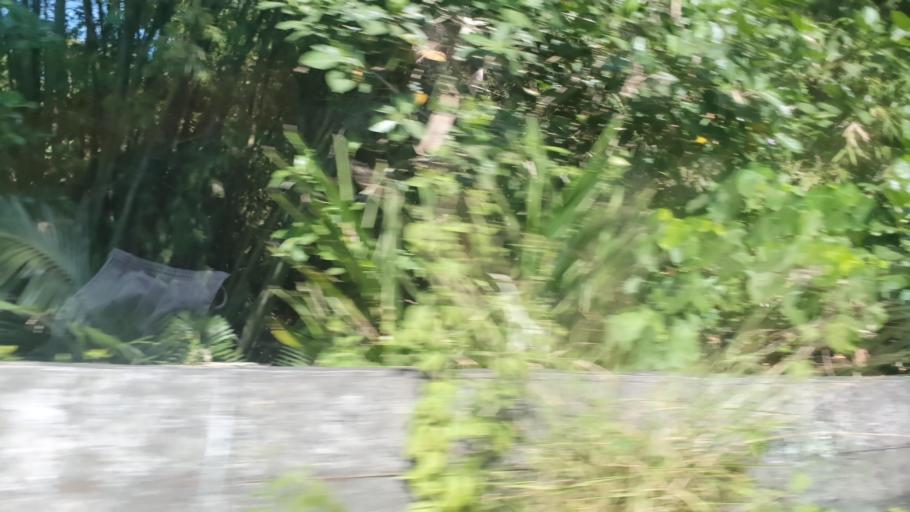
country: TW
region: Taiwan
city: Yujing
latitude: 23.0607
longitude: 120.3804
